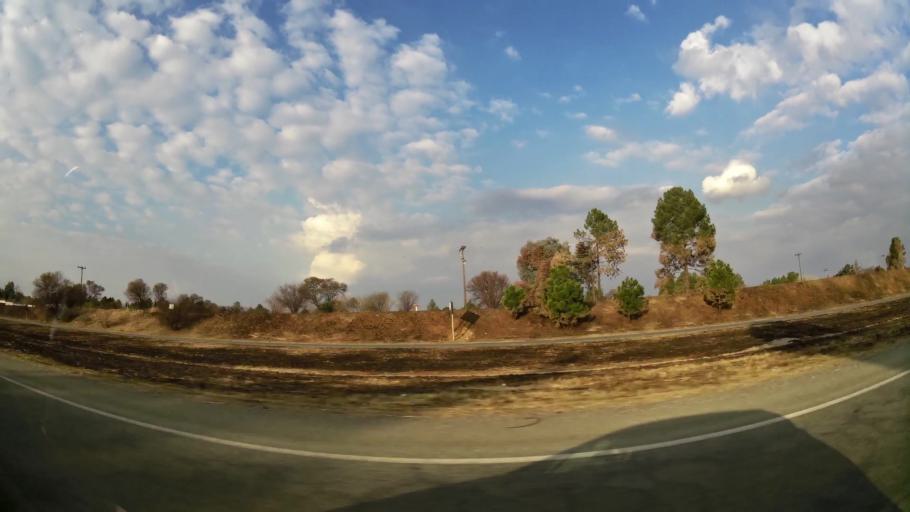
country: ZA
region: Gauteng
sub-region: Sedibeng District Municipality
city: Vanderbijlpark
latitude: -26.7559
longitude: 27.8252
